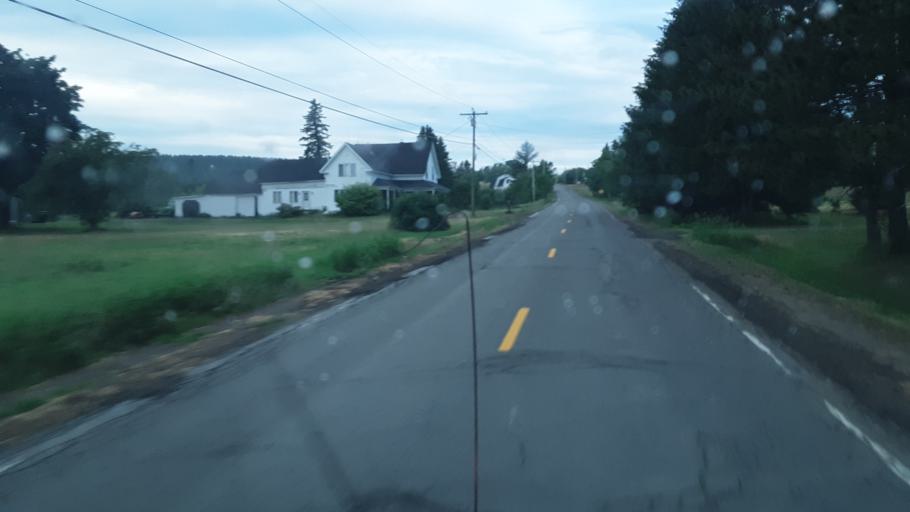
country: US
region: Maine
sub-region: Aroostook County
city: Presque Isle
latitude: 46.7338
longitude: -68.1811
